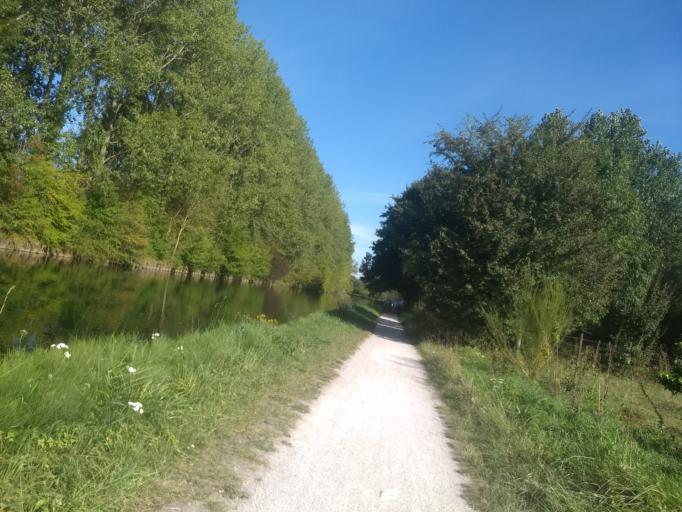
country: FR
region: Nord-Pas-de-Calais
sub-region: Departement du Pas-de-Calais
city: Feuchy
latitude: 50.2960
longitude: 2.8547
